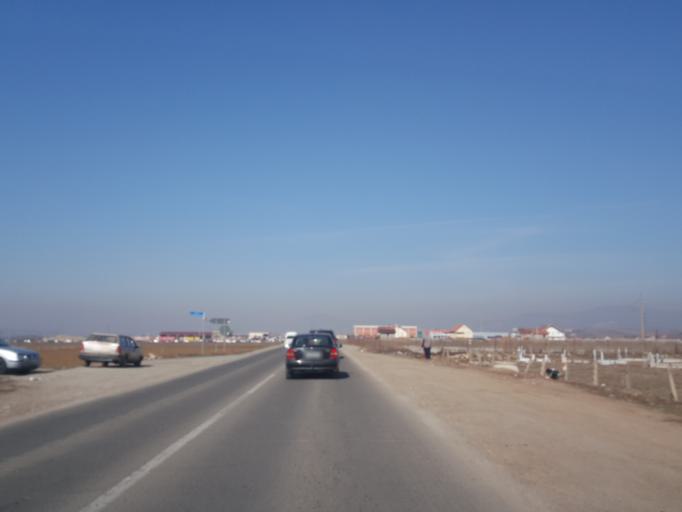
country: XK
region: Mitrovica
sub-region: Vushtrri
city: Vushtrri
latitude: 42.7876
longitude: 21.0074
